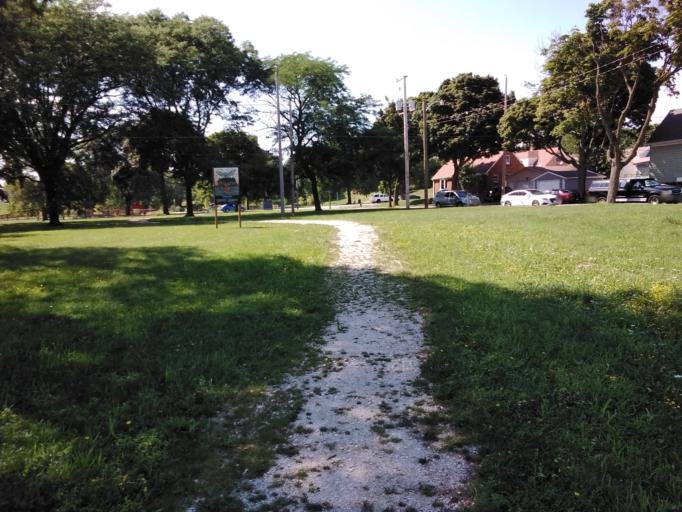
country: US
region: Wisconsin
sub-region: Milwaukee County
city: West Milwaukee
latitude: 42.9974
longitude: -87.9325
